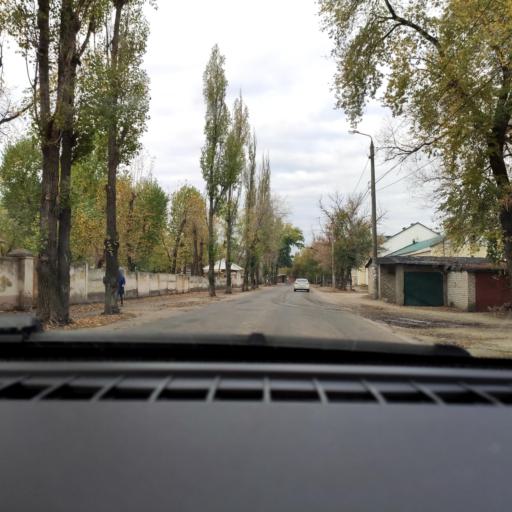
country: RU
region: Voronezj
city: Maslovka
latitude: 51.6153
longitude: 39.2468
